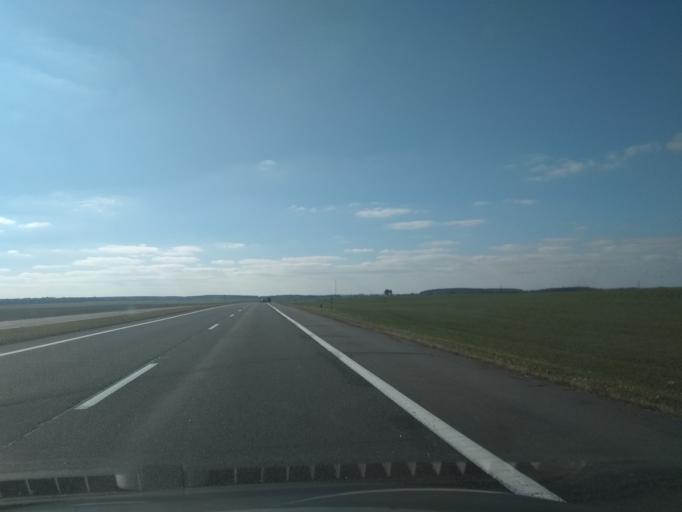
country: BY
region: Minsk
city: Snow
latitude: 53.3085
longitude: 26.3888
